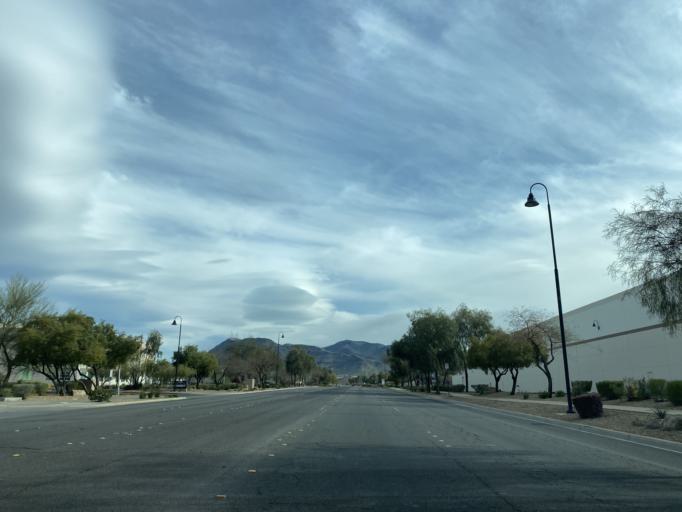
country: US
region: Nevada
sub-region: Clark County
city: Henderson
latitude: 36.0524
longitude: -115.0199
